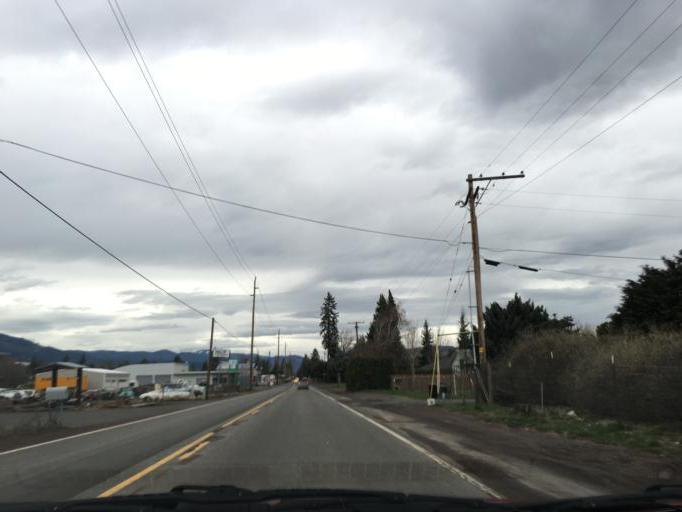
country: US
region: Oregon
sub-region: Hood River County
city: Hood River
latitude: 45.6799
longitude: -121.5289
